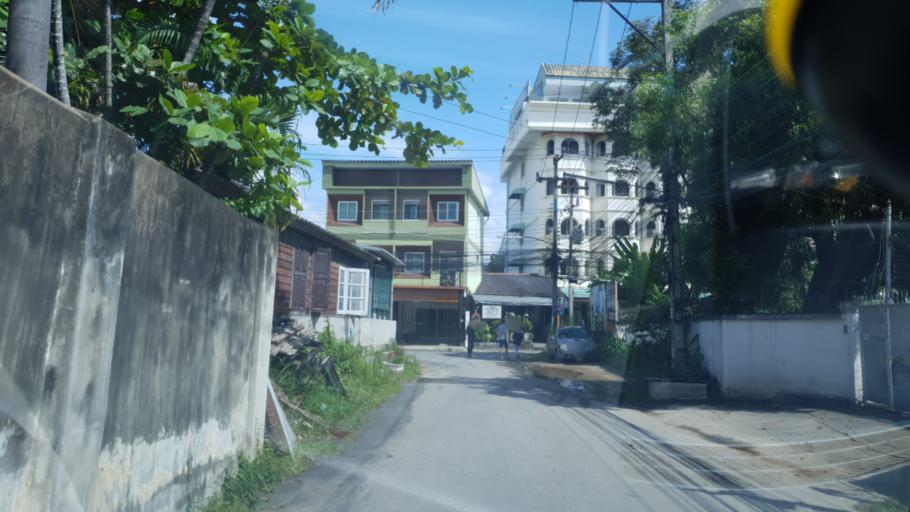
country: TH
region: Chiang Mai
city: Chiang Mai
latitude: 18.7865
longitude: 98.9681
